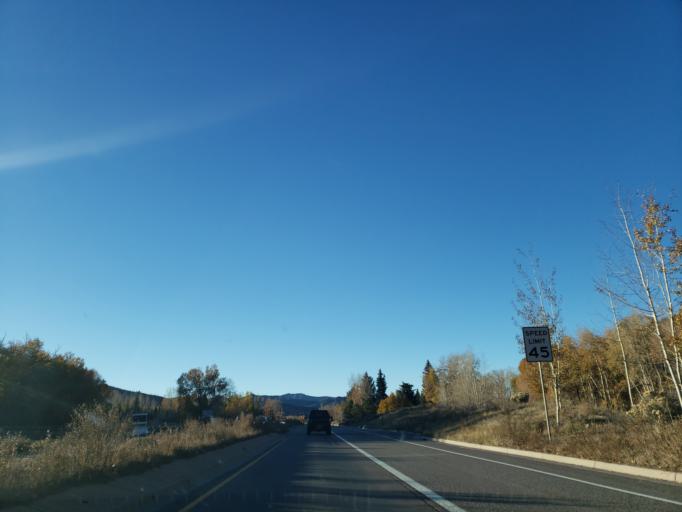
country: US
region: Colorado
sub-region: Pitkin County
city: Aspen
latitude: 39.1976
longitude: -106.8432
